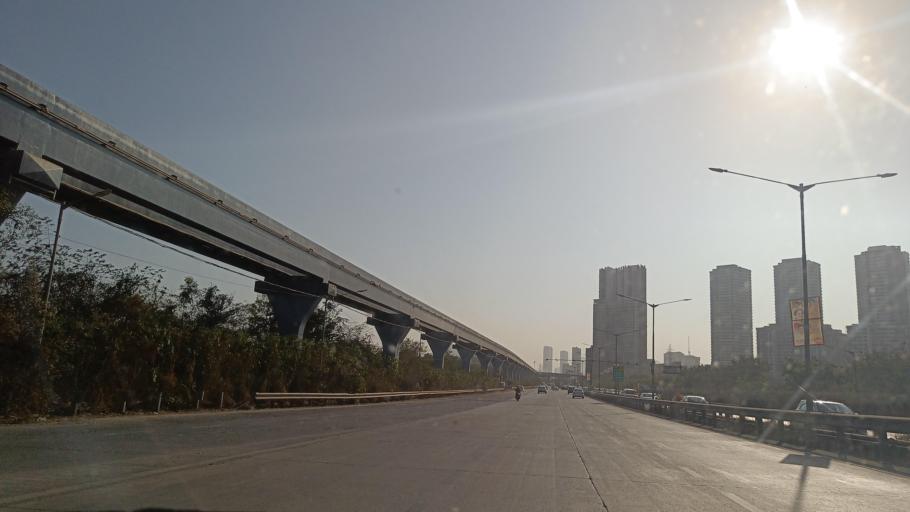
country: IN
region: Maharashtra
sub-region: Mumbai Suburban
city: Mumbai
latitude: 19.0277
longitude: 72.8859
